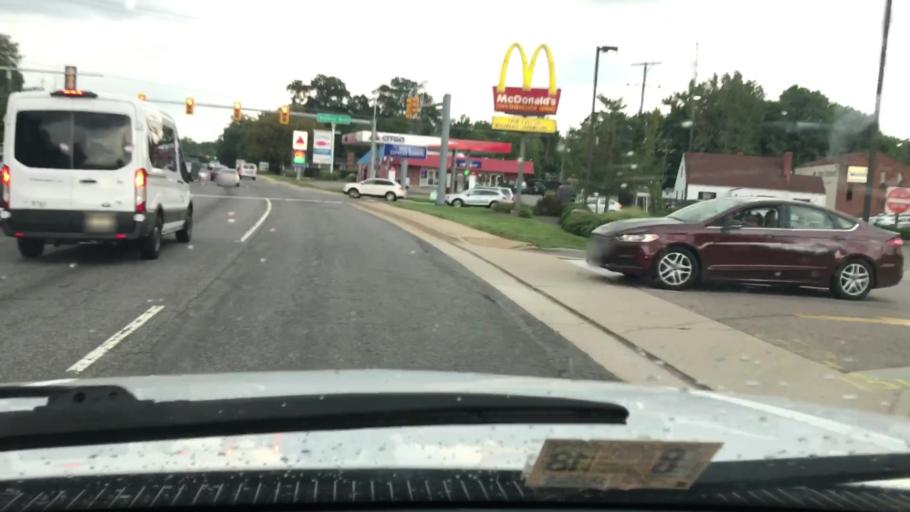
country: US
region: Virginia
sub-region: Henrico County
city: Dumbarton
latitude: 37.6182
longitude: -77.4991
